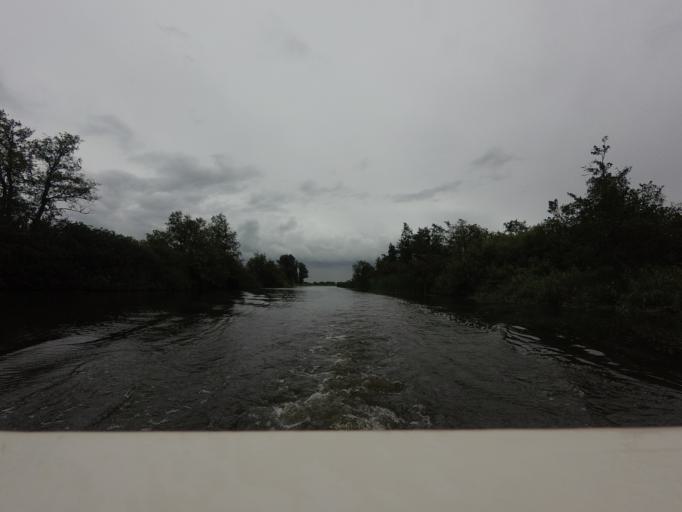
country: NL
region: Friesland
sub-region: Gemeente Boarnsterhim
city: Warten
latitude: 53.1179
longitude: 5.9324
